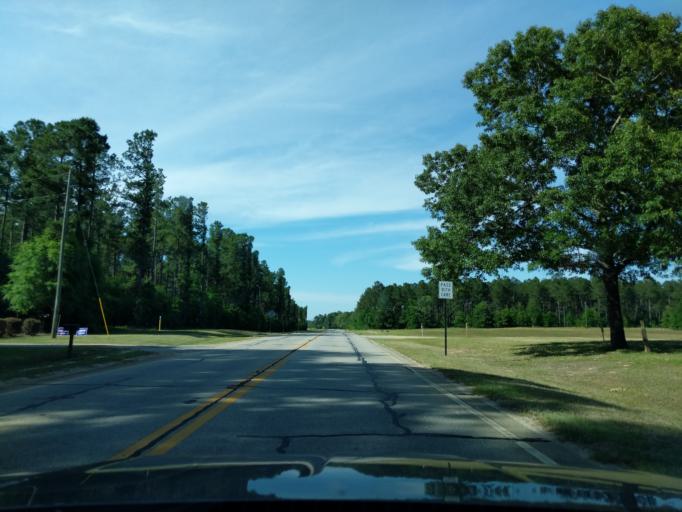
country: US
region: Georgia
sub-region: Jefferson County
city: Wrens
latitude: 33.2571
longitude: -82.3861
